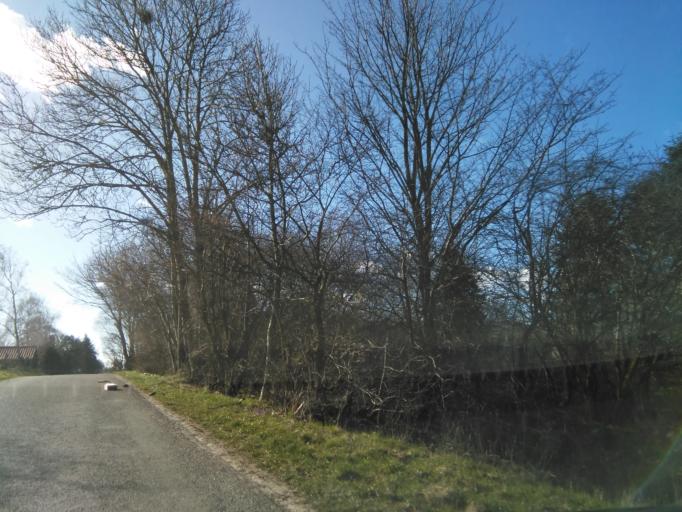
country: DK
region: Central Jutland
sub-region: Arhus Kommune
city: Beder
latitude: 56.0482
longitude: 10.2317
